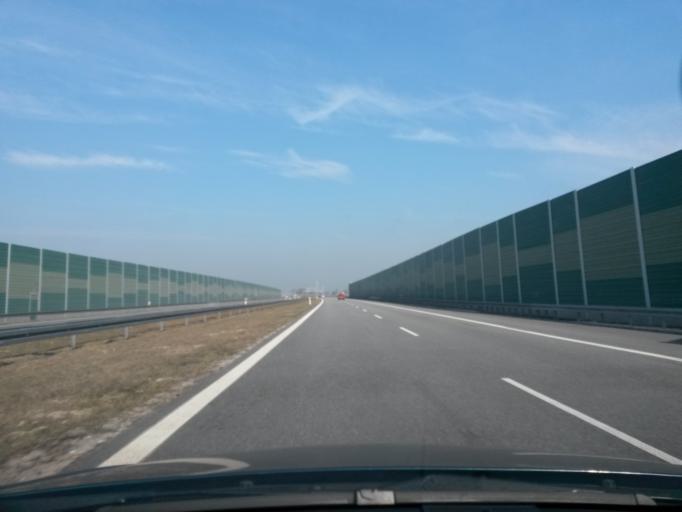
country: PL
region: Lodz Voivodeship
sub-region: Powiat kutnowski
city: Krzyzanow
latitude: 52.2022
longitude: 19.4851
